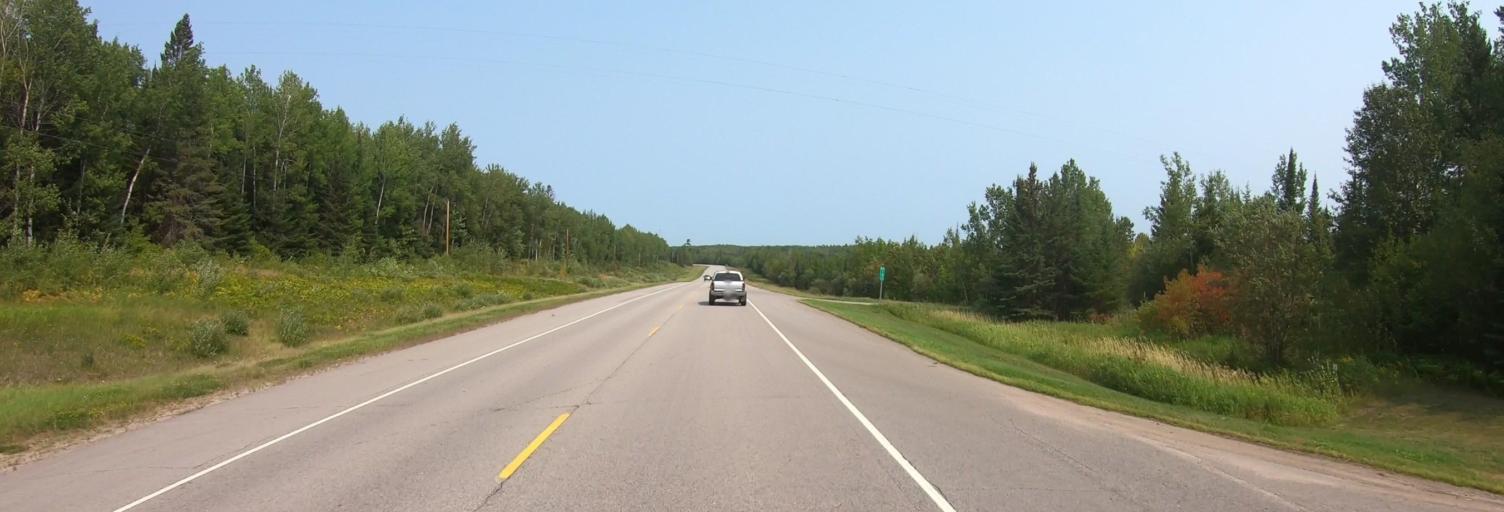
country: CA
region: Ontario
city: Fort Frances
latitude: 48.3192
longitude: -92.9623
